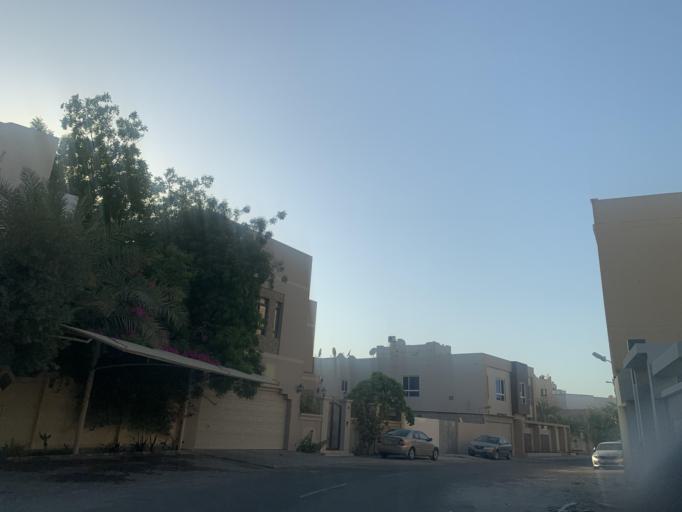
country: BH
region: Northern
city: Madinat `Isa
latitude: 26.1899
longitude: 50.4809
